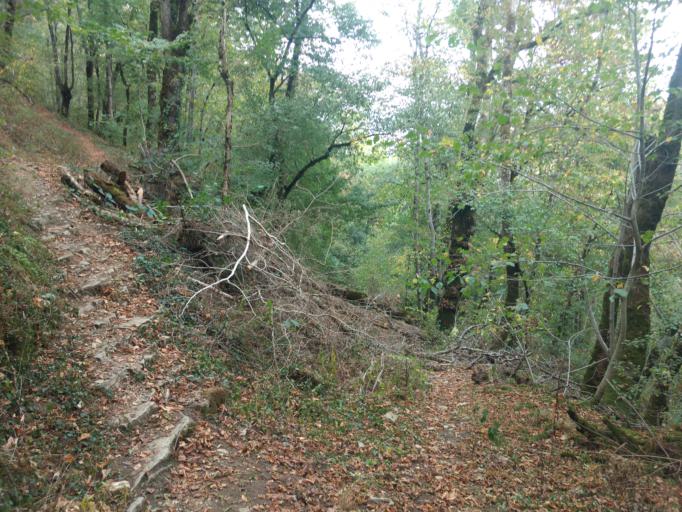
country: FR
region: Midi-Pyrenees
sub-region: Departement de l'Aveyron
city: Bozouls
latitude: 44.4711
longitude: 2.6931
